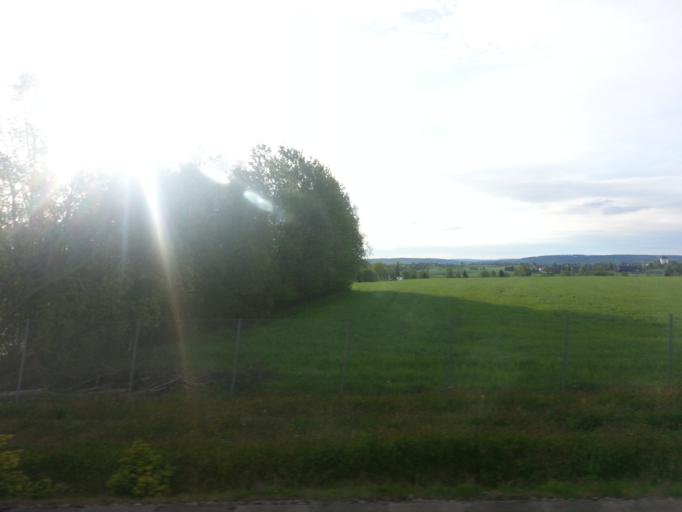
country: NO
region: Akershus
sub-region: Ullensaker
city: Klofta
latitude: 60.0916
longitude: 11.1408
